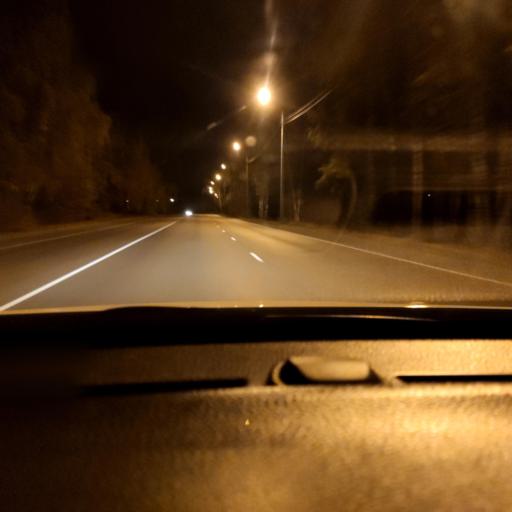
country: RU
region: Voronezj
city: Voronezh
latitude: 51.6772
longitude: 39.2734
